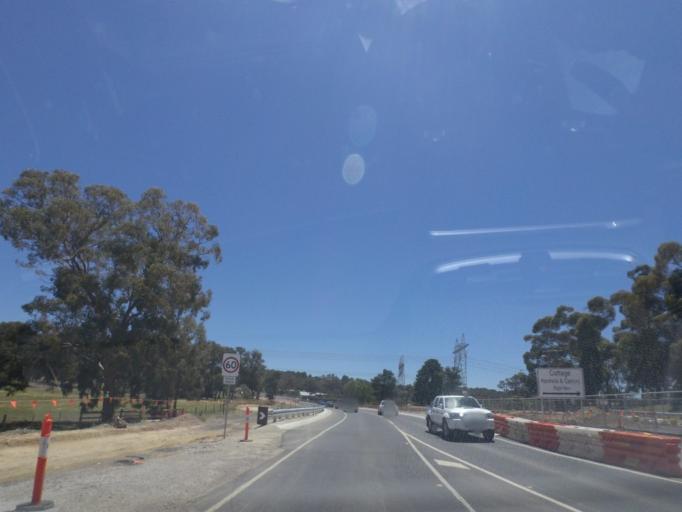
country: AU
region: Victoria
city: Plenty
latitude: -37.6582
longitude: 145.1254
